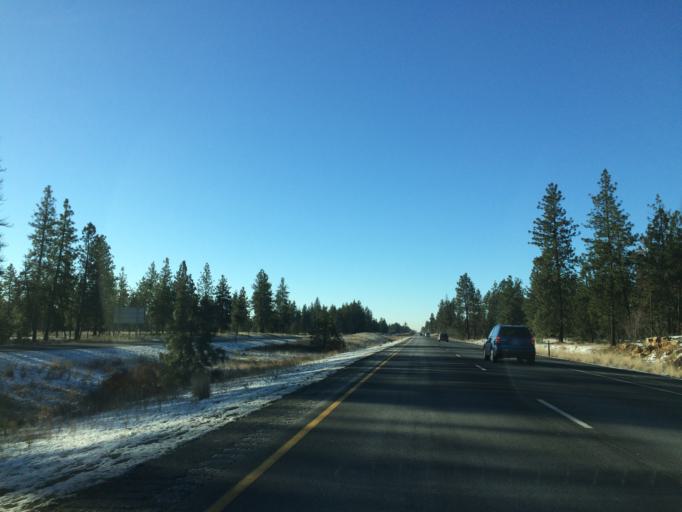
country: US
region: Washington
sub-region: Spokane County
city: Medical Lake
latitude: 47.4977
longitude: -117.7008
